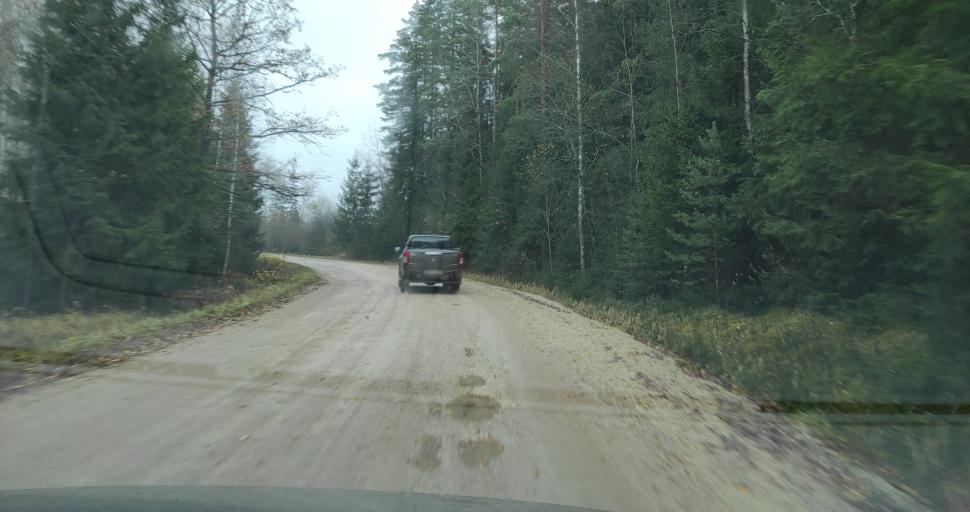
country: LV
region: Skrunda
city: Skrunda
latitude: 56.6852
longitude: 22.0739
